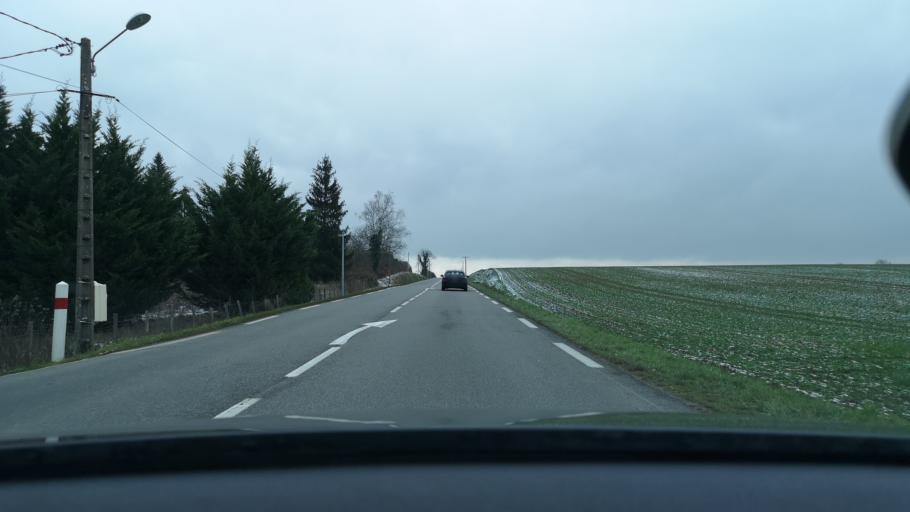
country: FR
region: Bourgogne
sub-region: Departement de Saone-et-Loire
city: Saint-Martin-en-Bresse
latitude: 46.7488
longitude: 5.0447
